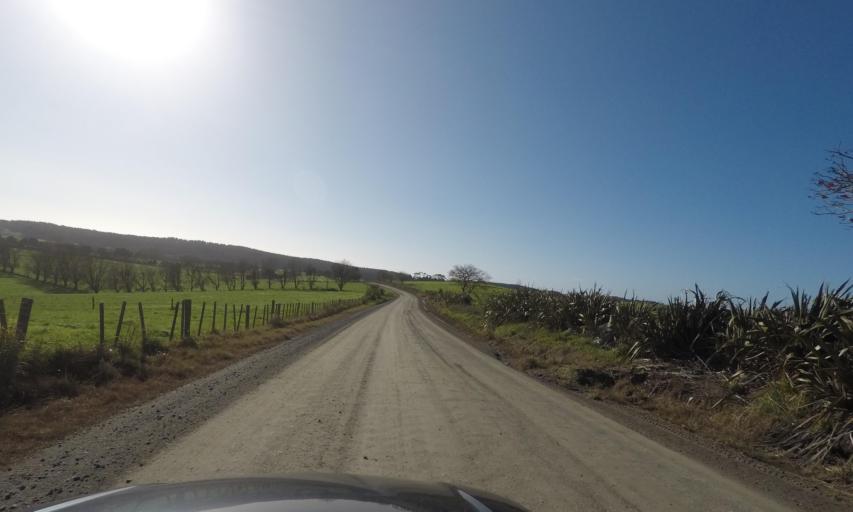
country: NZ
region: Auckland
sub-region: Auckland
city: Wellsford
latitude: -36.1611
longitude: 174.6082
